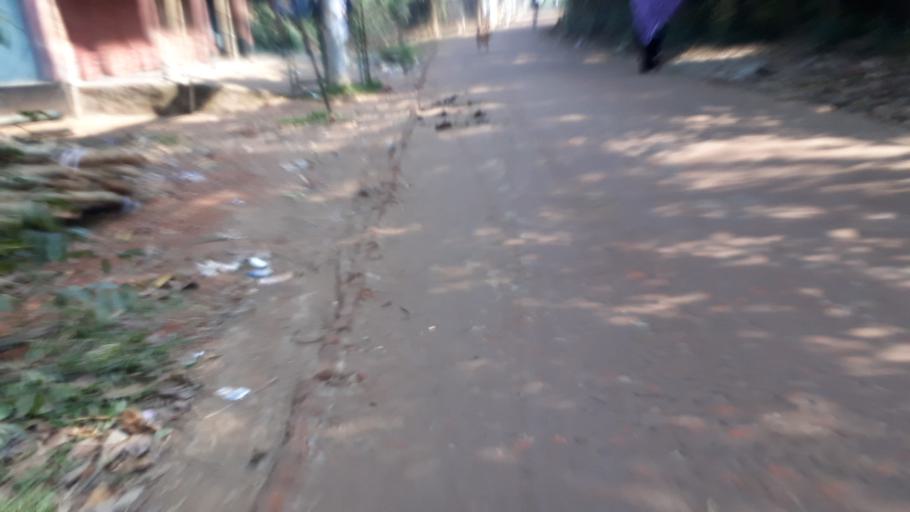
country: BD
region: Dhaka
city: Tungi
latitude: 23.8554
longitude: 90.3044
